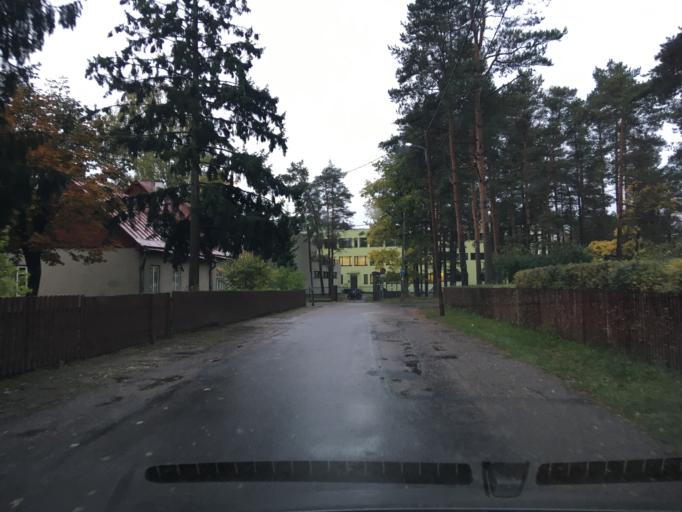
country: EE
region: Harju
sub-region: Tallinna linn
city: Tallinn
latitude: 59.3839
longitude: 24.7034
